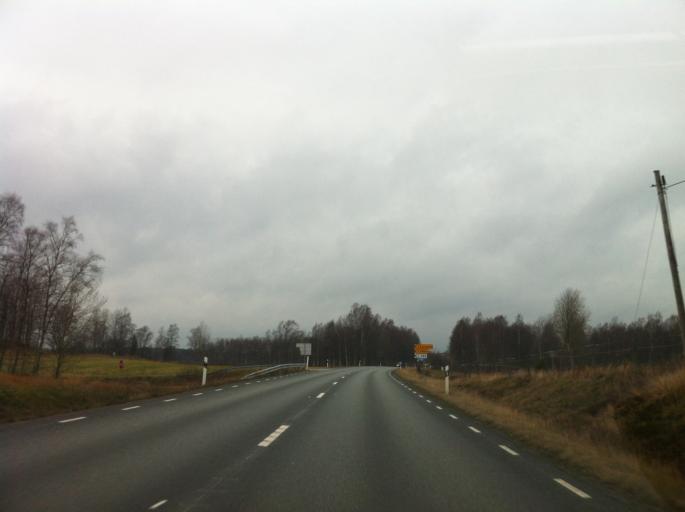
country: SE
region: Joenkoeping
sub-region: Savsjo Kommun
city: Saevsjoe
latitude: 57.3930
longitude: 14.7233
